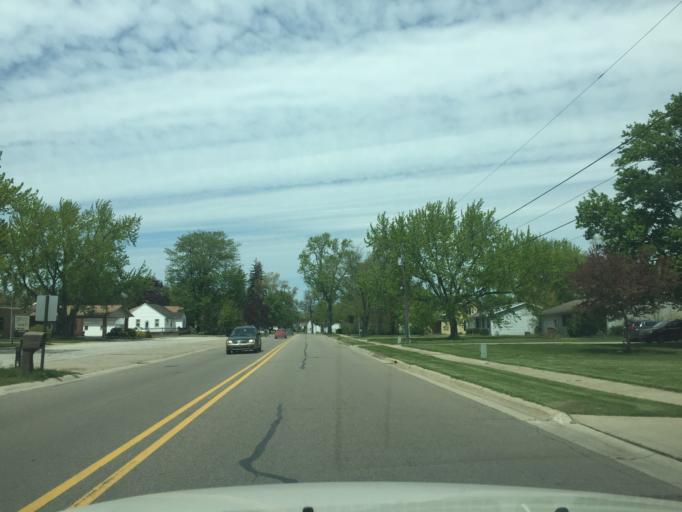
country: US
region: Michigan
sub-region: Berrien County
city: Stevensville
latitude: 42.0096
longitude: -86.5191
